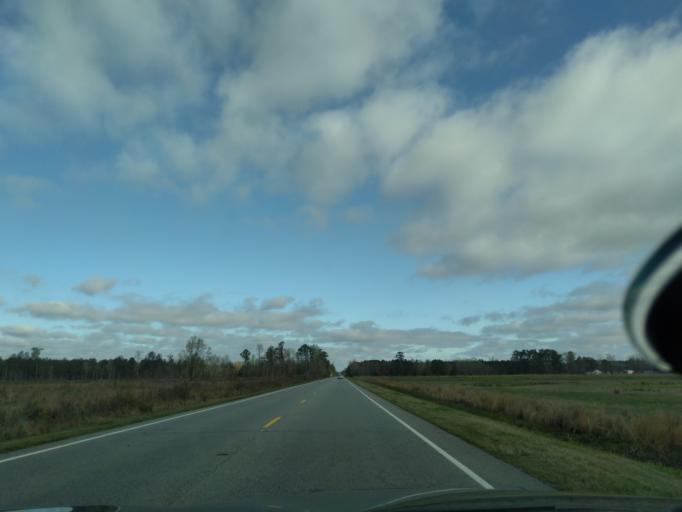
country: US
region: North Carolina
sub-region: Washington County
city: Plymouth
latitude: 35.9946
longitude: -76.7708
